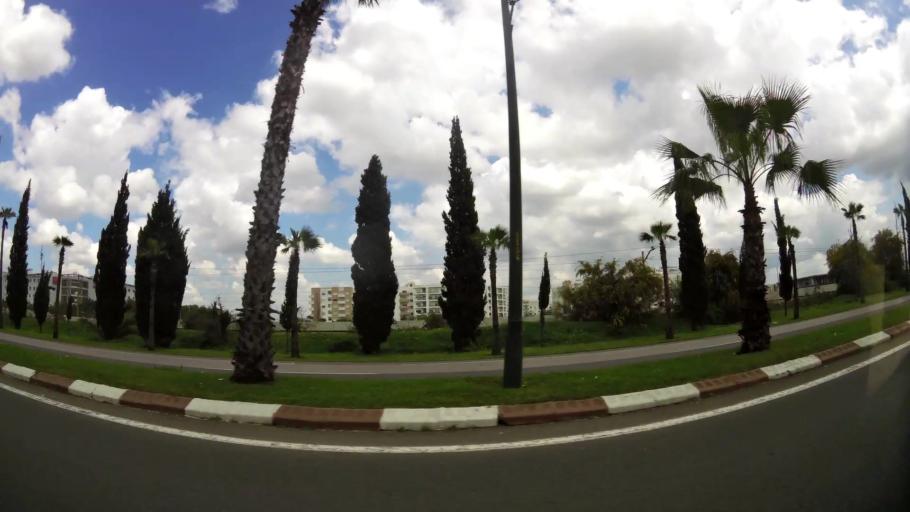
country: MA
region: Chaouia-Ouardigha
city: Nouaseur
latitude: 33.3916
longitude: -7.5670
